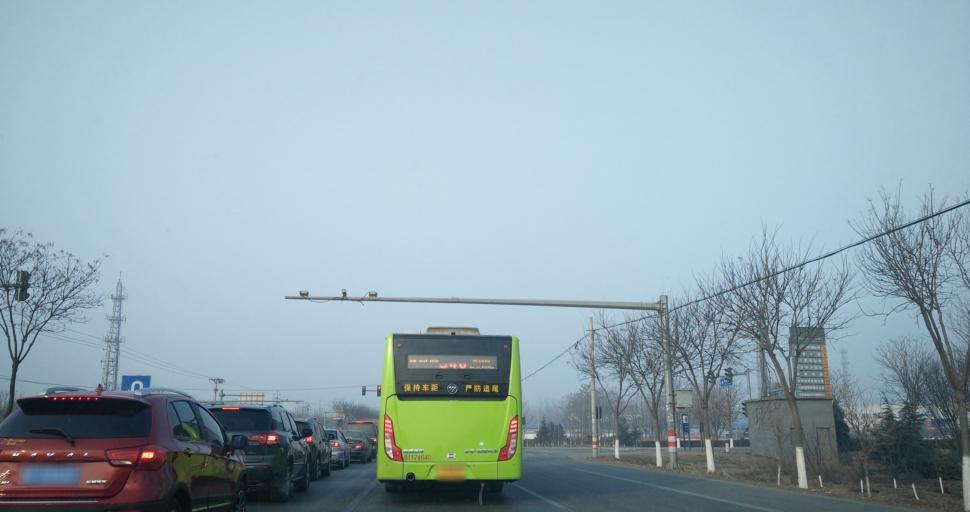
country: CN
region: Beijing
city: Yinghai
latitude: 39.7146
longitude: 116.4027
